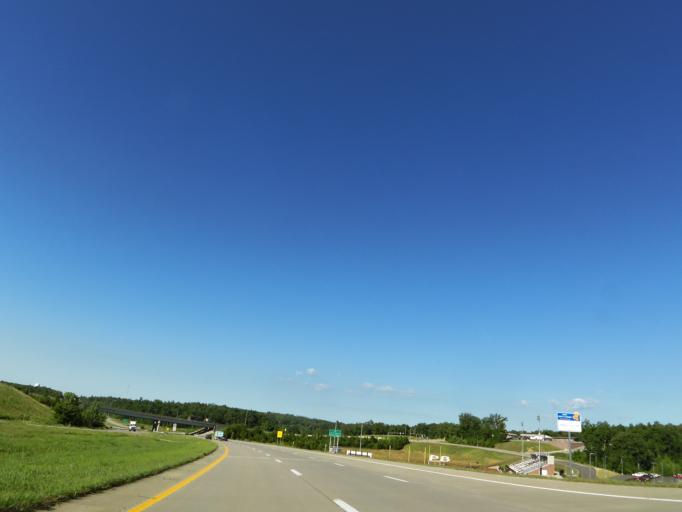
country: US
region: Missouri
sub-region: Butler County
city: Poplar Bluff
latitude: 36.7912
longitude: -90.4480
